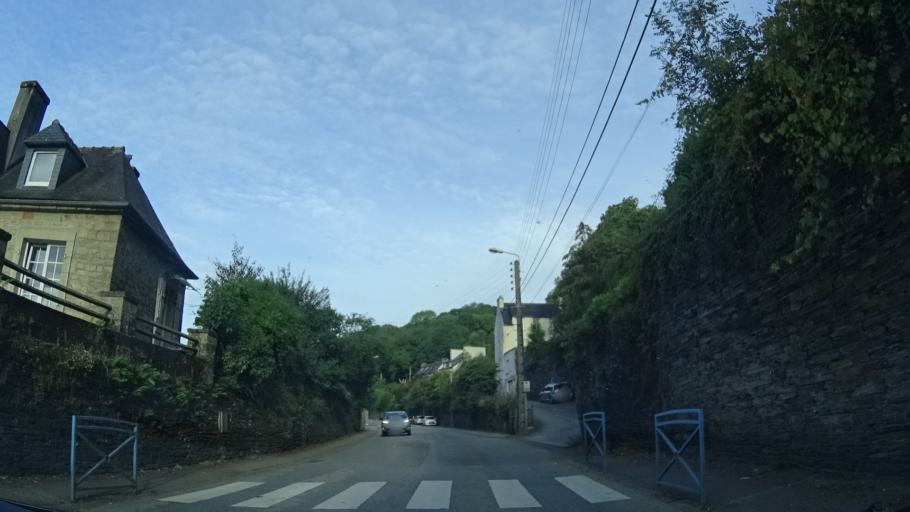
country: FR
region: Brittany
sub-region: Departement du Finistere
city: Chateaulin
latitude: 48.1983
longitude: -4.0927
